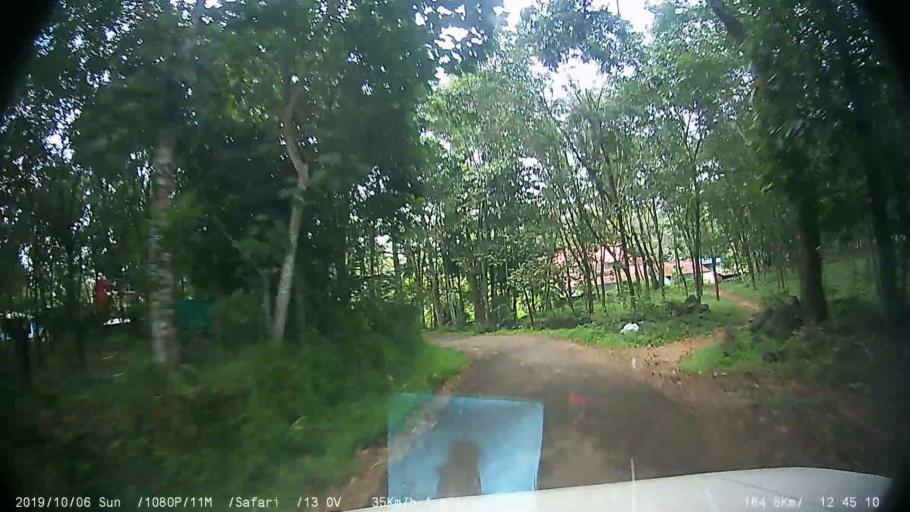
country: IN
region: Kerala
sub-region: Kottayam
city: Palackattumala
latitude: 9.7717
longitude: 76.6130
